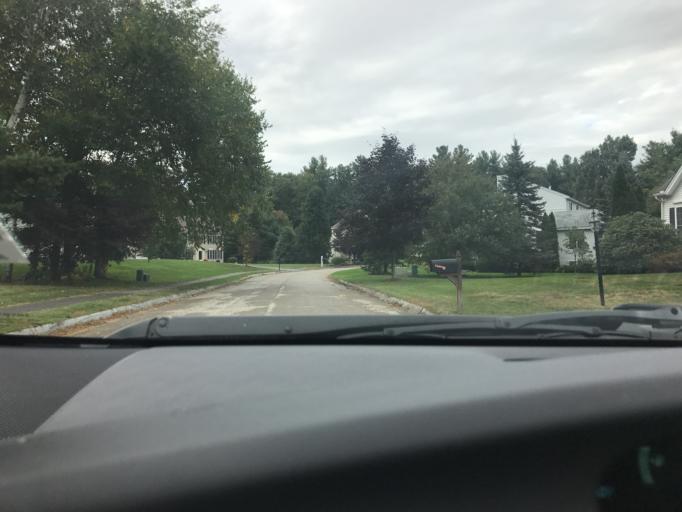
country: US
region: Massachusetts
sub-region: Middlesex County
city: Littleton Common
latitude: 42.5659
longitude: -71.4765
